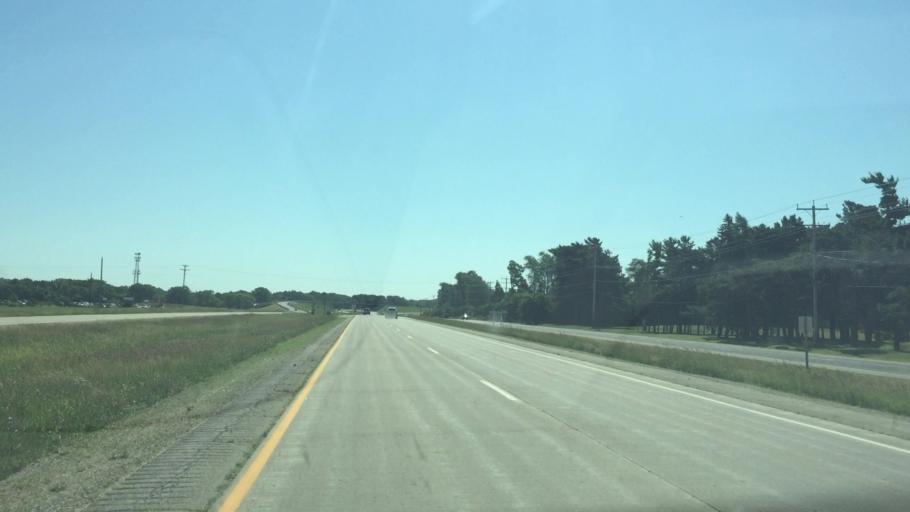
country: US
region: Wisconsin
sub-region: Outagamie County
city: Kimberly
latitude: 44.2075
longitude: -88.3461
